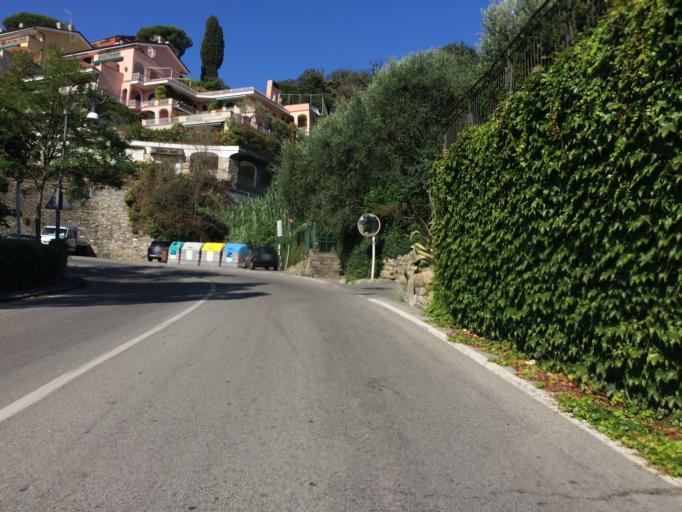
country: IT
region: Liguria
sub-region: Provincia di Genova
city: Santa Margherita Ligure
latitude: 44.3444
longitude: 9.2143
